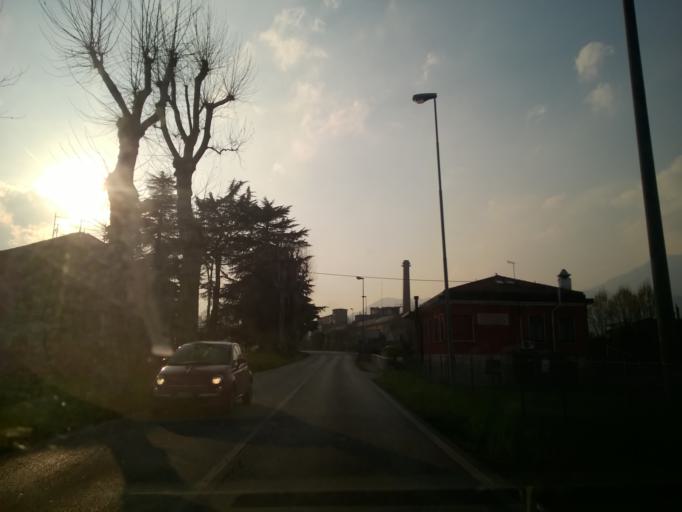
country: IT
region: Veneto
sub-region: Provincia di Vicenza
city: Schio
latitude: 45.7108
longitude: 11.3795
